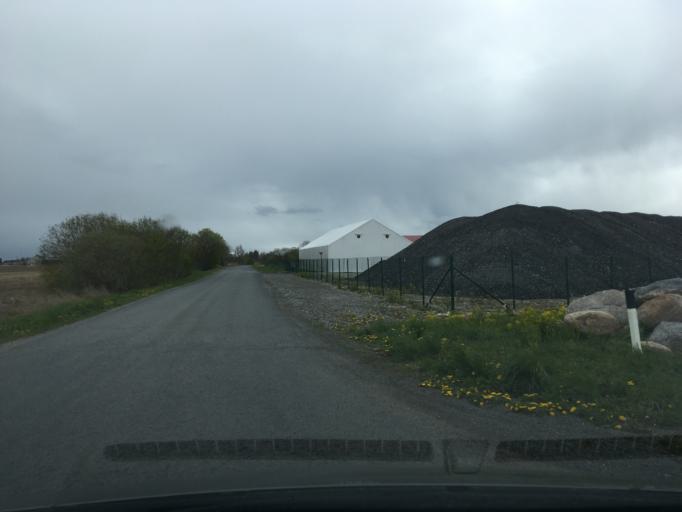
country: EE
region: Harju
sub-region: Rae vald
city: Vaida
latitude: 59.2995
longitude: 24.9718
